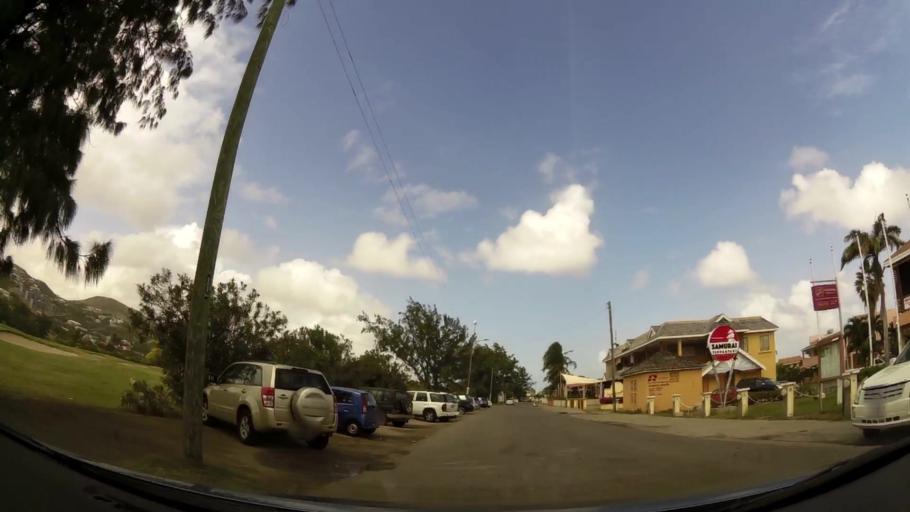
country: KN
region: Saint George Basseterre
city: Basseterre
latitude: 17.2863
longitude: -62.6857
